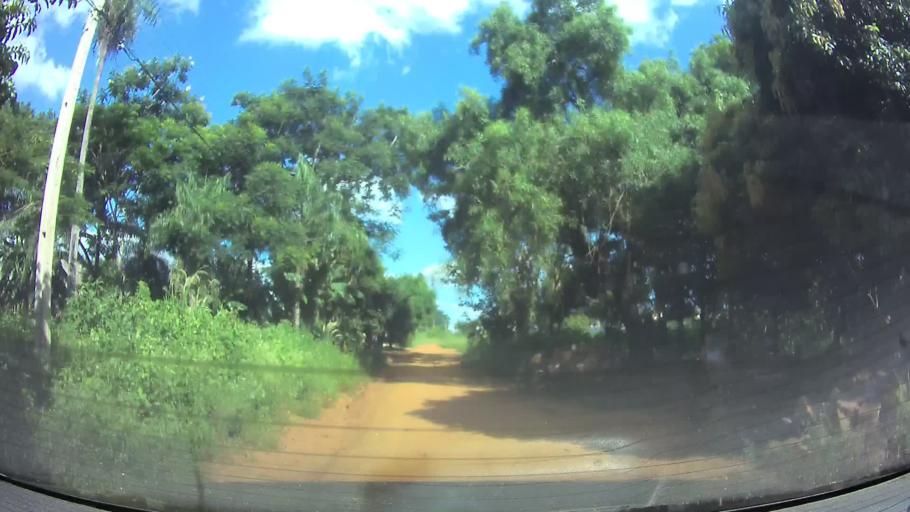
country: PY
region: Central
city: Itaugua
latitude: -25.3881
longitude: -57.3447
